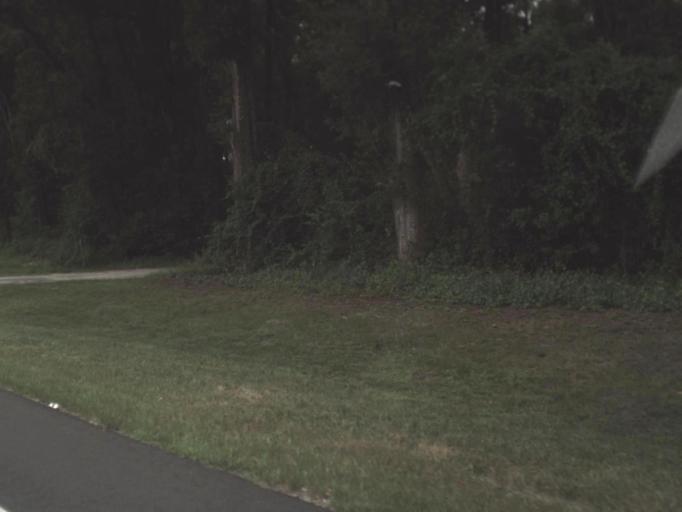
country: US
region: Florida
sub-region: Pasco County
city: Lacoochee
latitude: 28.4573
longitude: -82.1887
